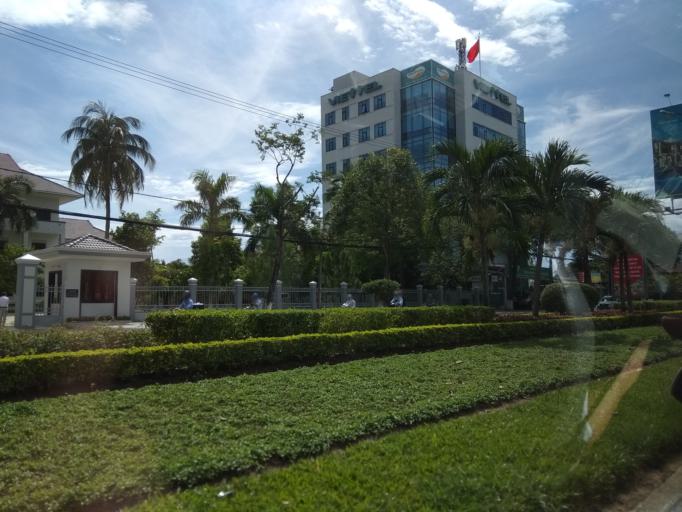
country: VN
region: Quang Nam
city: Tam Ky
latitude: 15.5694
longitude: 108.4754
